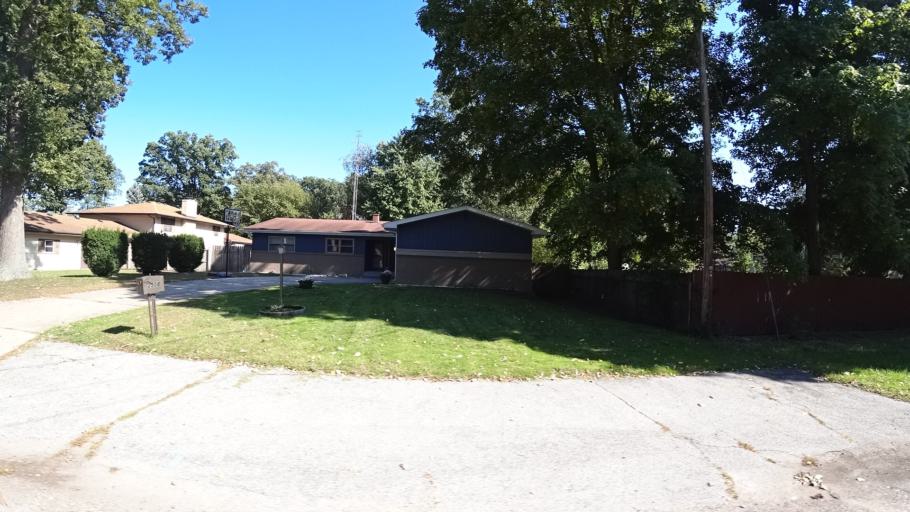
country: US
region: Indiana
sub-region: LaPorte County
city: Michigan City
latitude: 41.6942
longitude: -86.8890
